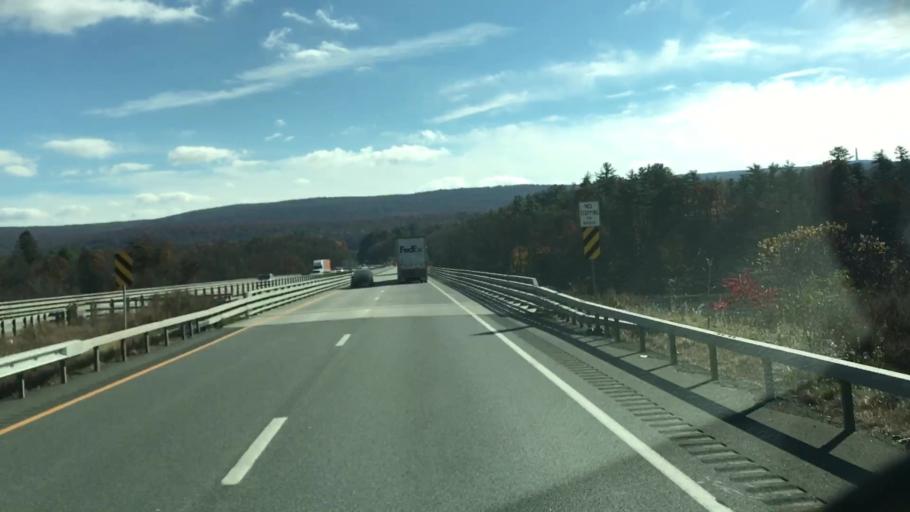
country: US
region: Pennsylvania
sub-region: Pike County
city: Matamoras
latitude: 41.3585
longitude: -74.6976
